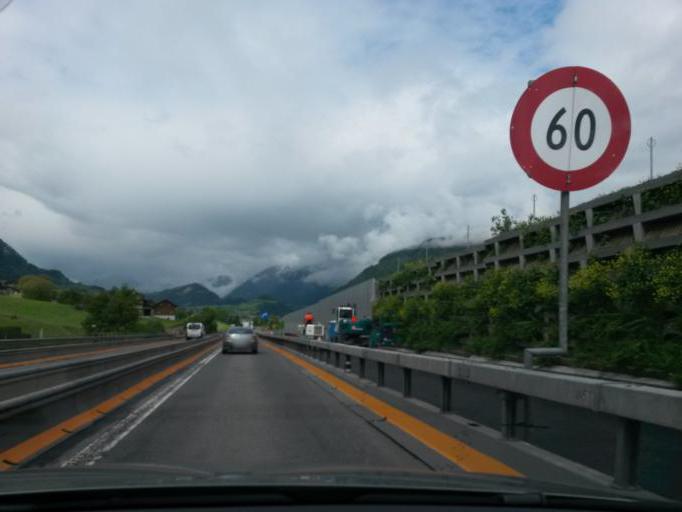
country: CH
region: Nidwalden
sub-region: Nidwalden
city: Buochs
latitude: 46.9701
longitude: 8.4129
